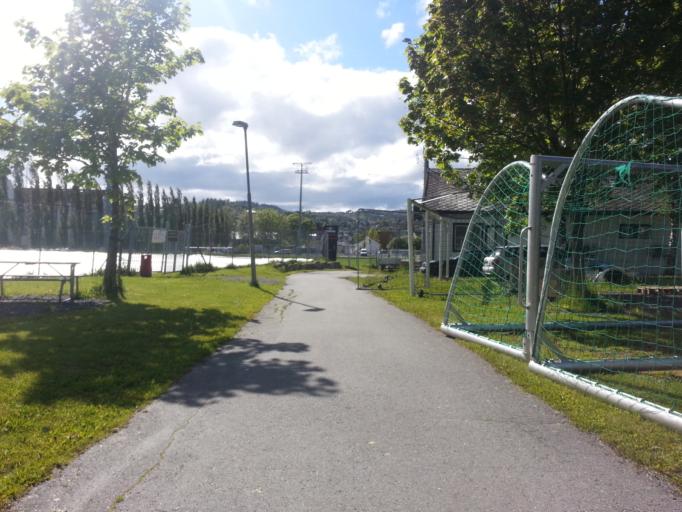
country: NO
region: Sor-Trondelag
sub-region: Trondheim
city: Trondheim
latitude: 63.4104
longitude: 10.4058
